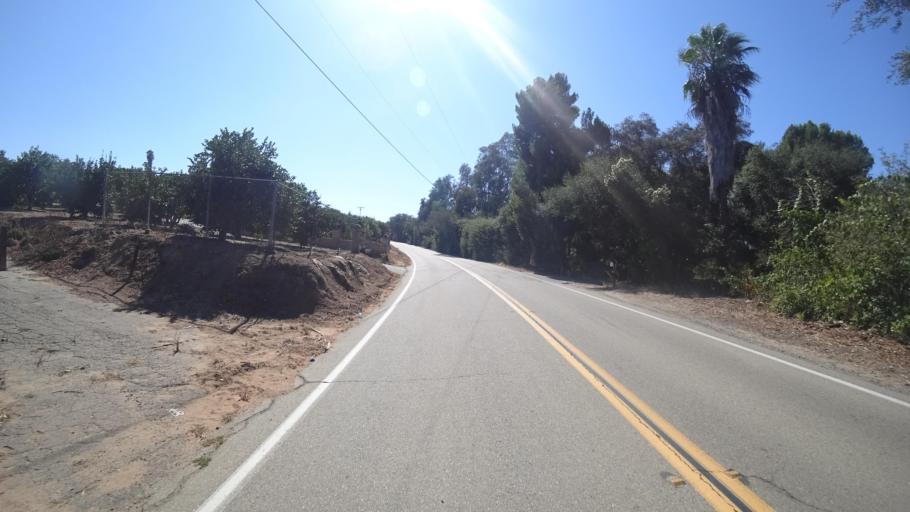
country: US
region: California
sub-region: San Diego County
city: Bonsall
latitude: 33.2983
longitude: -117.1654
